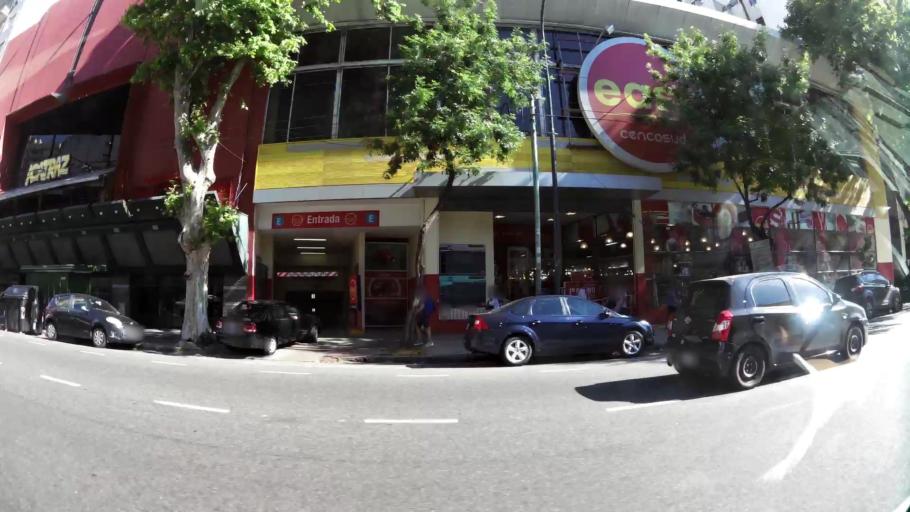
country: AR
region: Buenos Aires F.D.
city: Buenos Aires
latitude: -34.6111
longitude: -58.4181
